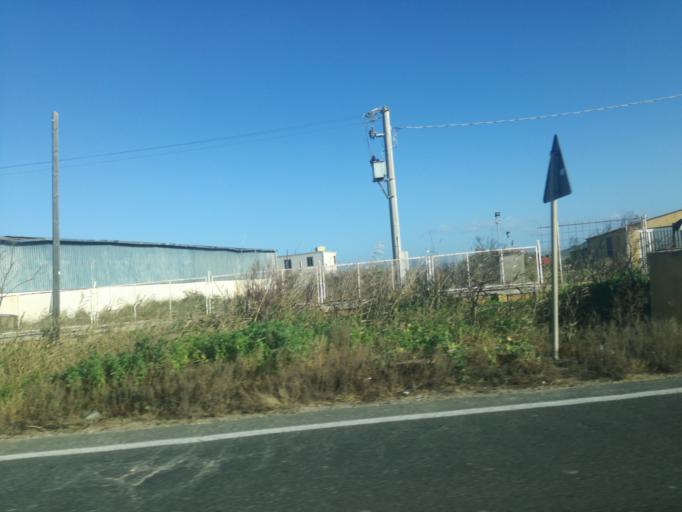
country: IT
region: Sicily
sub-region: Provincia di Caltanissetta
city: Gela
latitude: 37.0553
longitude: 14.2985
